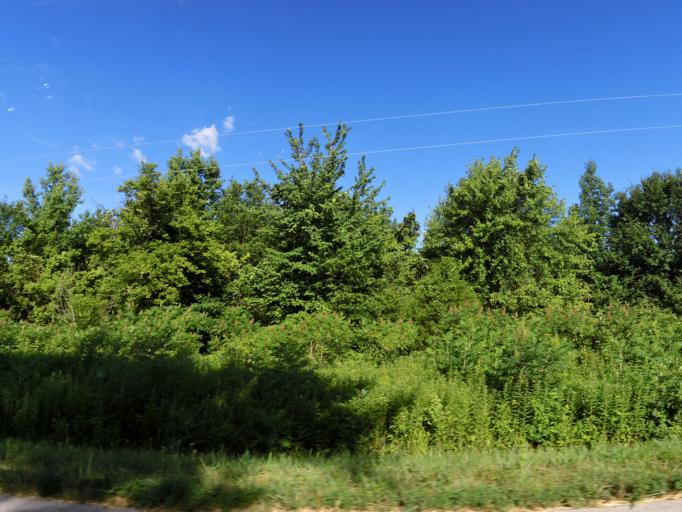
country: US
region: Missouri
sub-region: Butler County
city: Poplar Bluff
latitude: 36.6034
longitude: -90.5204
